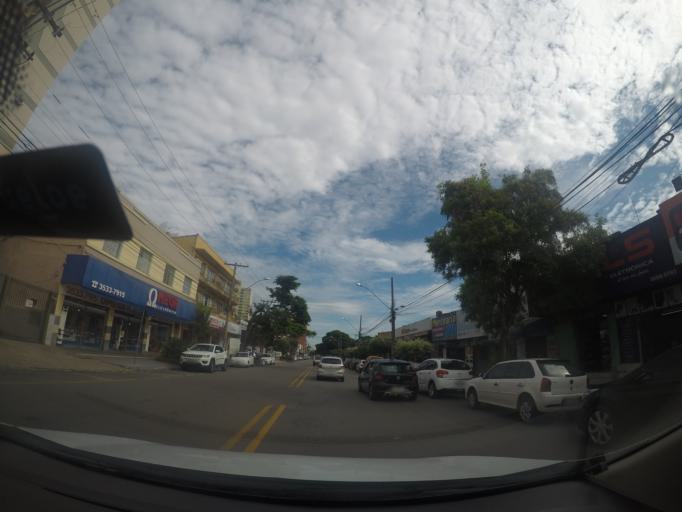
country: BR
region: Goias
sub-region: Goiania
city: Goiania
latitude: -16.6679
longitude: -49.2582
